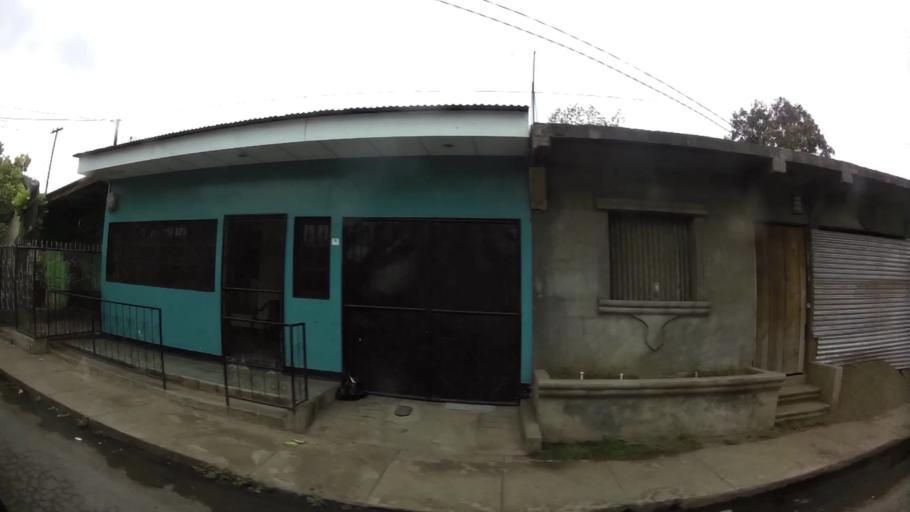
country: NI
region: Leon
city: Leon
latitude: 12.4456
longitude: -86.8656
